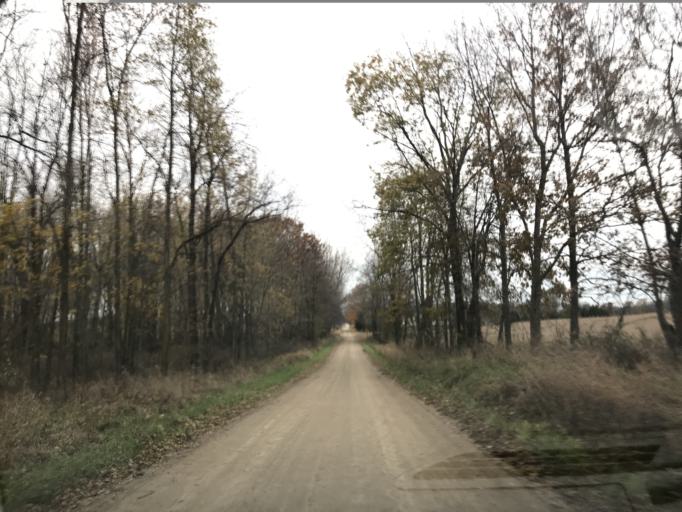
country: US
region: Michigan
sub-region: Lenawee County
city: Manitou Beach-Devils Lake
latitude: 42.0106
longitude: -84.3350
